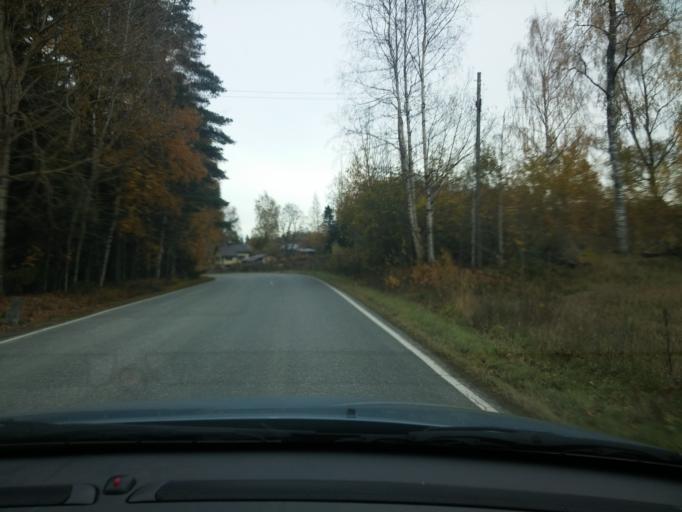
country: FI
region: Haeme
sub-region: Forssa
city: Tammela
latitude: 60.7647
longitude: 23.8661
